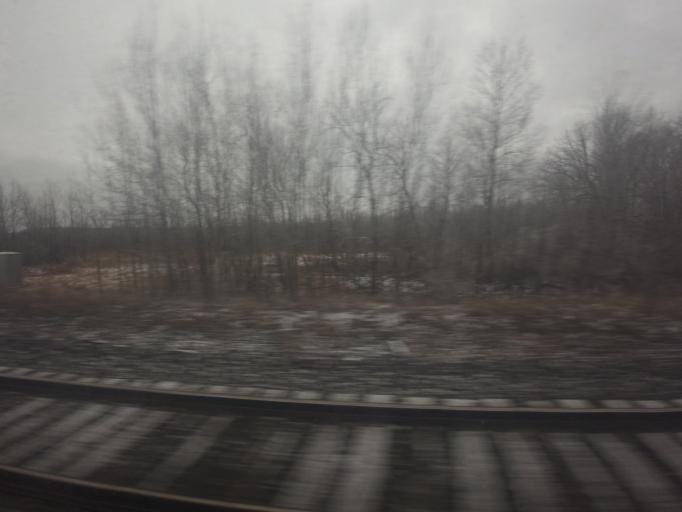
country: CA
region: Ontario
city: Gananoque
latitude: 44.3720
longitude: -76.1249
